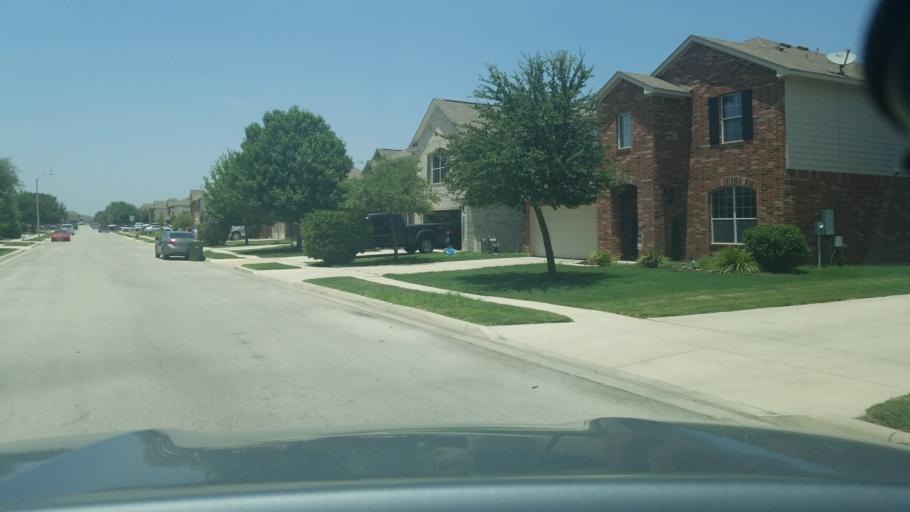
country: US
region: Texas
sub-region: Guadalupe County
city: Cibolo
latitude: 29.5744
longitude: -98.2278
